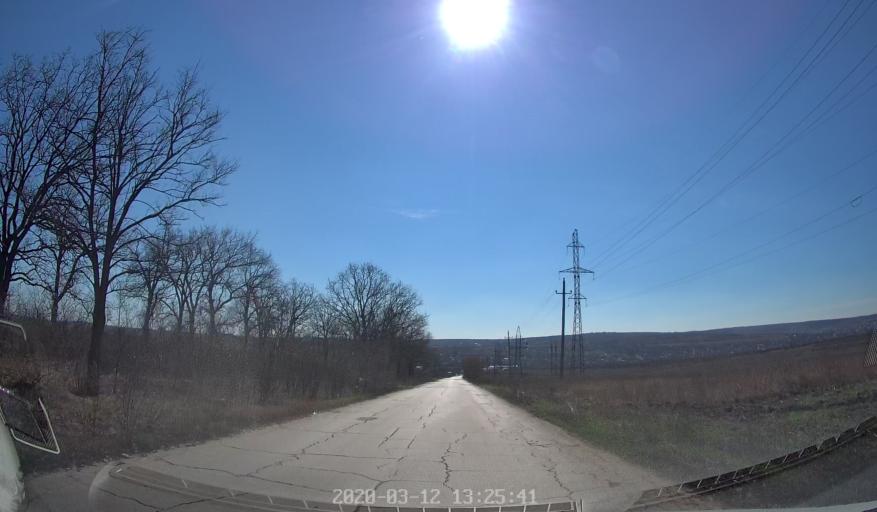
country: MD
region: Laloveni
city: Ialoveni
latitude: 46.9410
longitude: 28.8184
